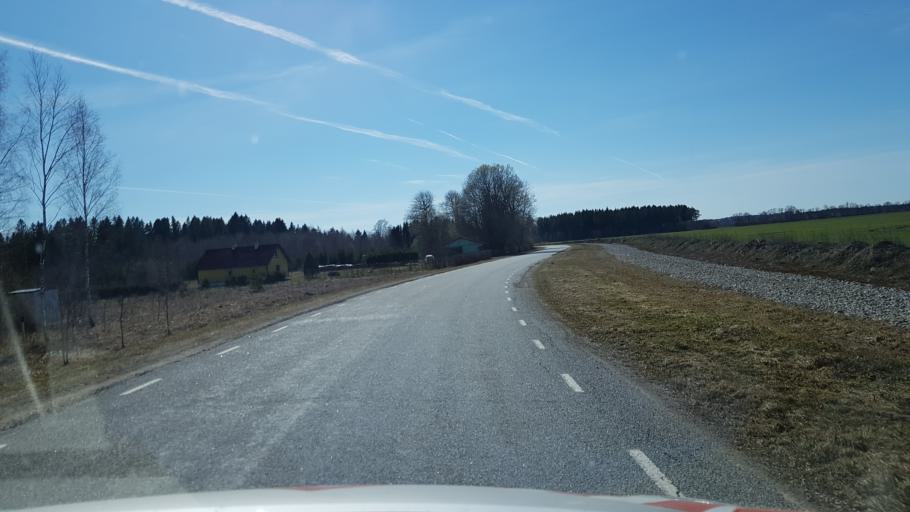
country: EE
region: Laeaene-Virumaa
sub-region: Viru-Nigula vald
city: Kunda
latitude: 59.3412
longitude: 26.6689
